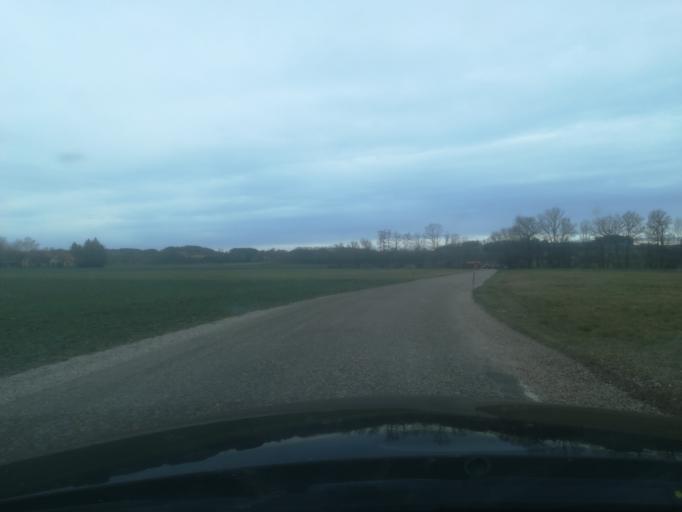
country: AT
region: Upper Austria
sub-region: Wels-Land
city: Gunskirchen
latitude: 48.1676
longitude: 13.9794
